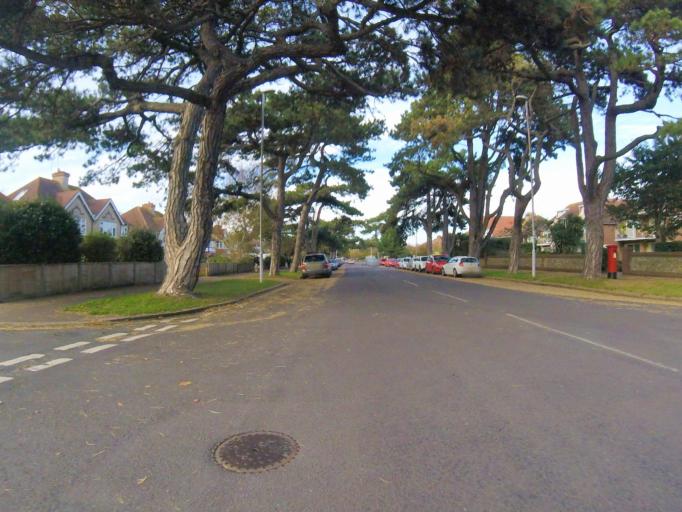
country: GB
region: England
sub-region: West Sussex
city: Worthing
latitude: 50.8165
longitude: -0.3942
